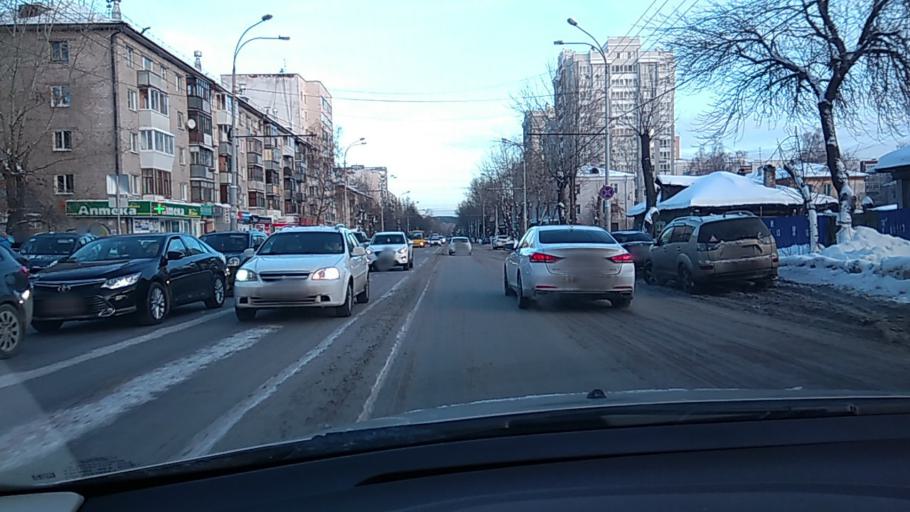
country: RU
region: Sverdlovsk
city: Yekaterinburg
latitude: 56.8090
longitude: 60.6143
